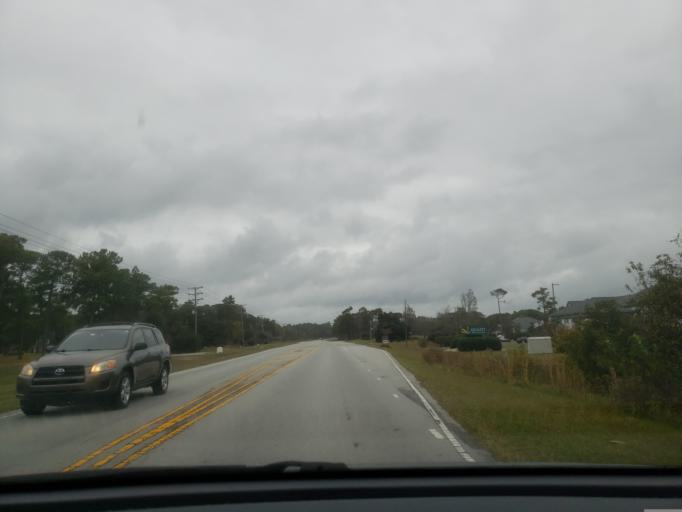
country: US
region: North Carolina
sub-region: Onslow County
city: Sneads Ferry
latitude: 34.5080
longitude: -77.4331
